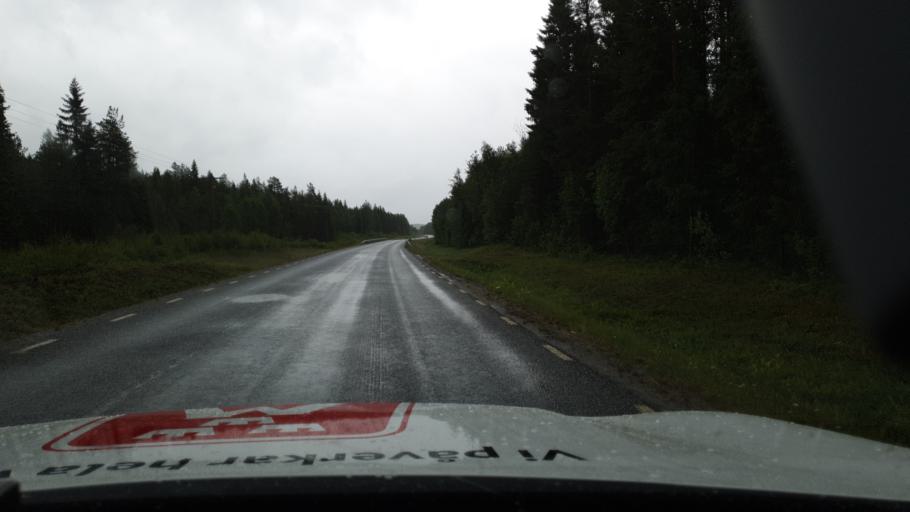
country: SE
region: Vaesterbotten
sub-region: Vilhelmina Kommun
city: Vilhelmina
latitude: 64.3990
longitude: 16.8526
